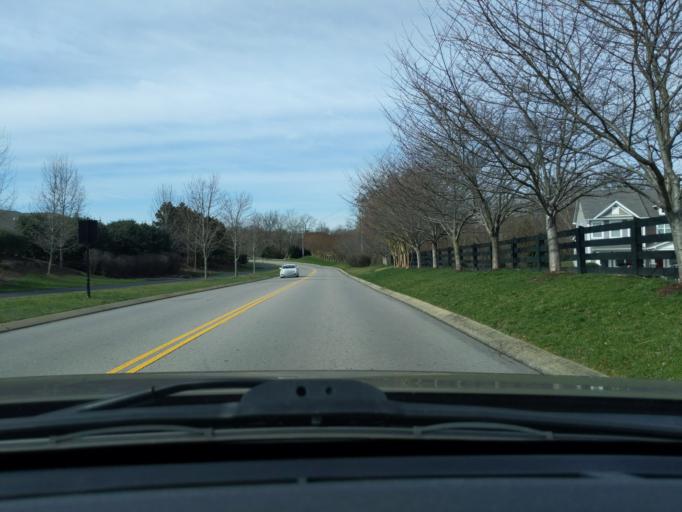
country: US
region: Tennessee
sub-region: Wilson County
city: Mount Juliet
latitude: 36.1674
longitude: -86.4831
